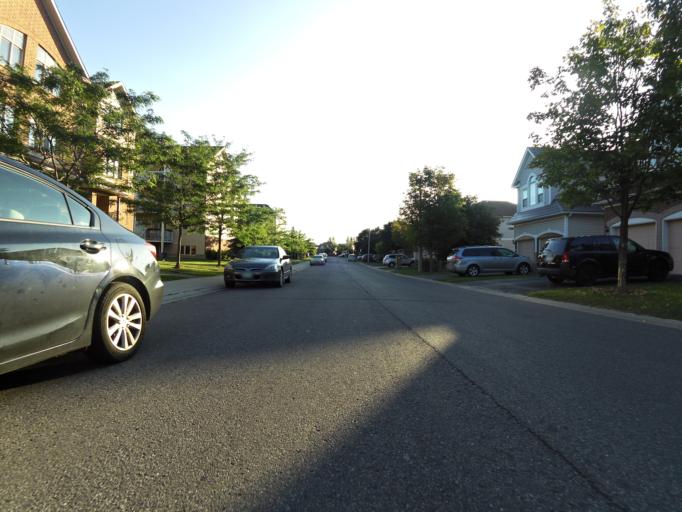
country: CA
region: Ontario
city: Bells Corners
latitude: 45.2743
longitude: -75.7414
